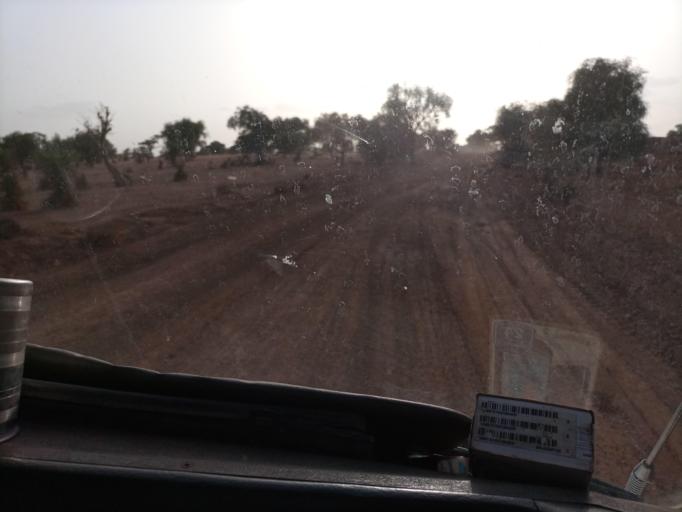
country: SN
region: Louga
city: Dara
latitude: 15.3557
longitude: -15.5347
